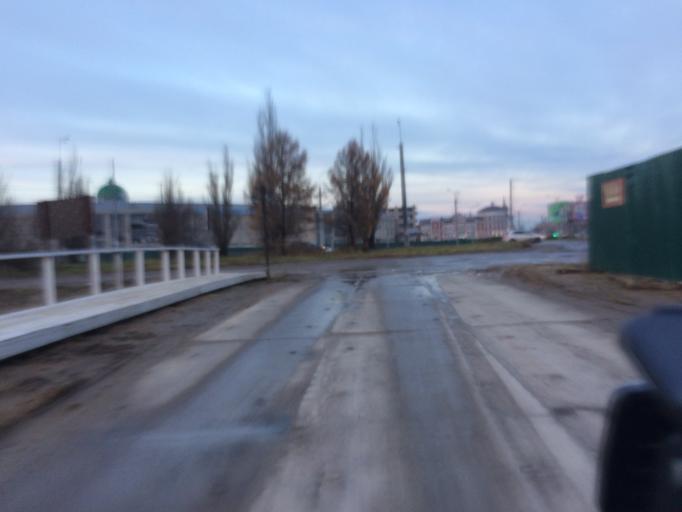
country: RU
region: Mariy-El
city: Yoshkar-Ola
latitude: 56.6270
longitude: 47.9029
